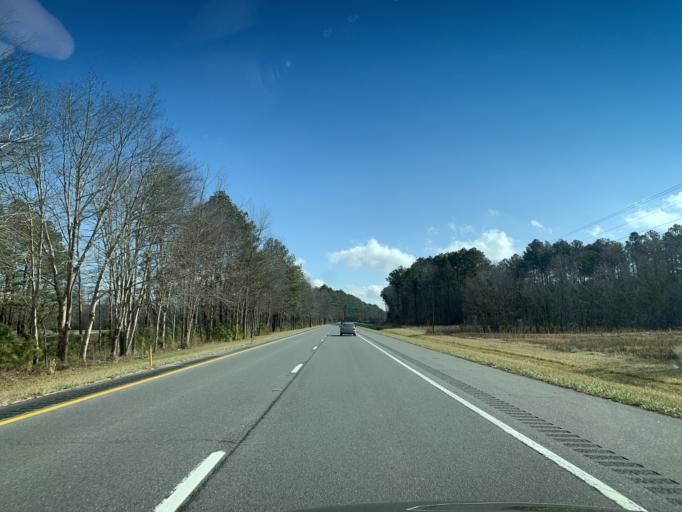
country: US
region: Maryland
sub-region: Worcester County
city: Berlin
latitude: 38.3795
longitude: -75.2920
